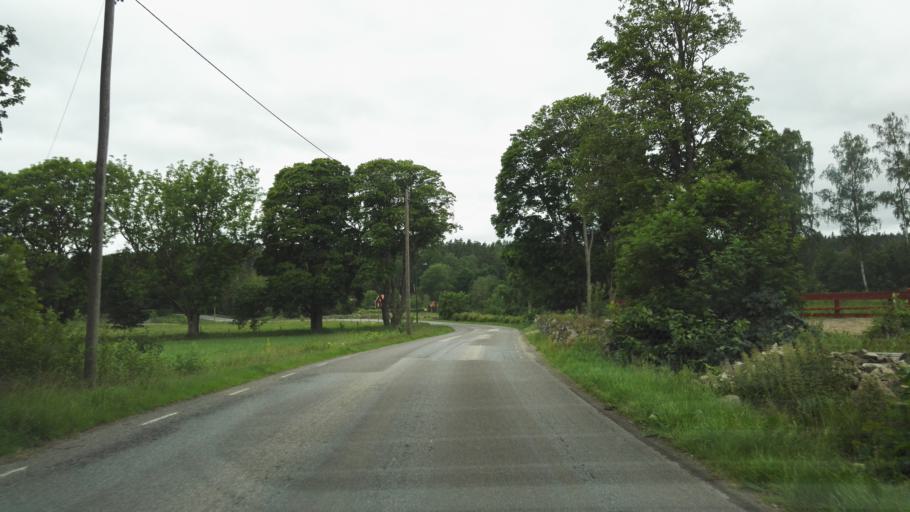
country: SE
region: Kronoberg
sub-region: Vaxjo Kommun
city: Rottne
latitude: 57.0922
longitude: 14.7967
